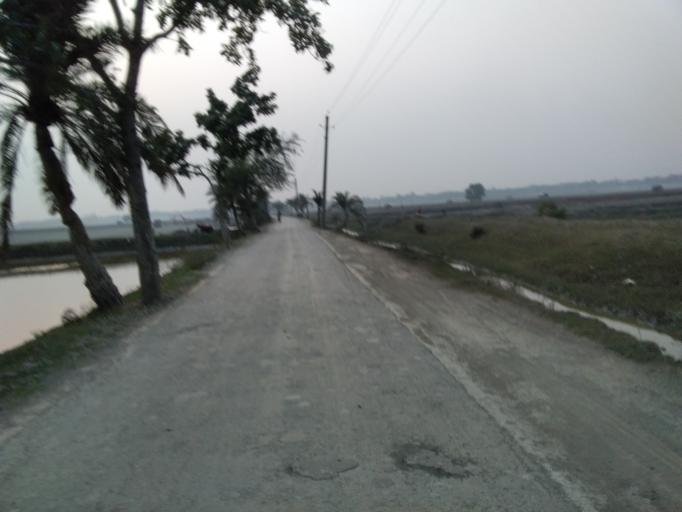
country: BD
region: Khulna
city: Satkhira
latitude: 22.6494
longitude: 89.0100
